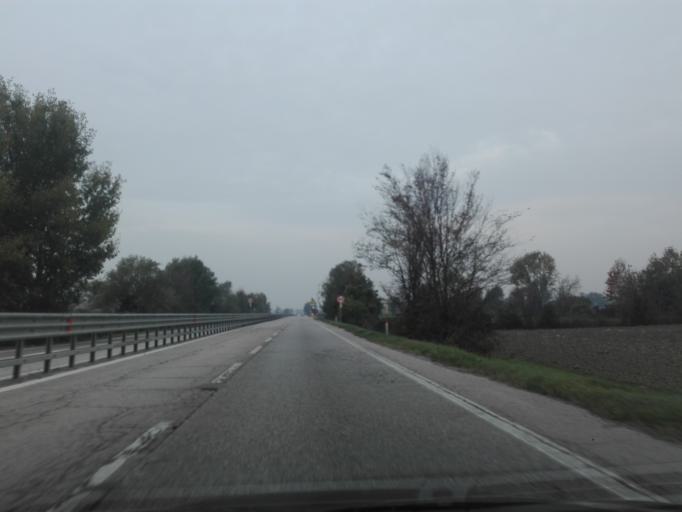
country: IT
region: Veneto
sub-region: Provincia di Rovigo
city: Arqua Polesine
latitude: 45.0217
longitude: 11.7215
